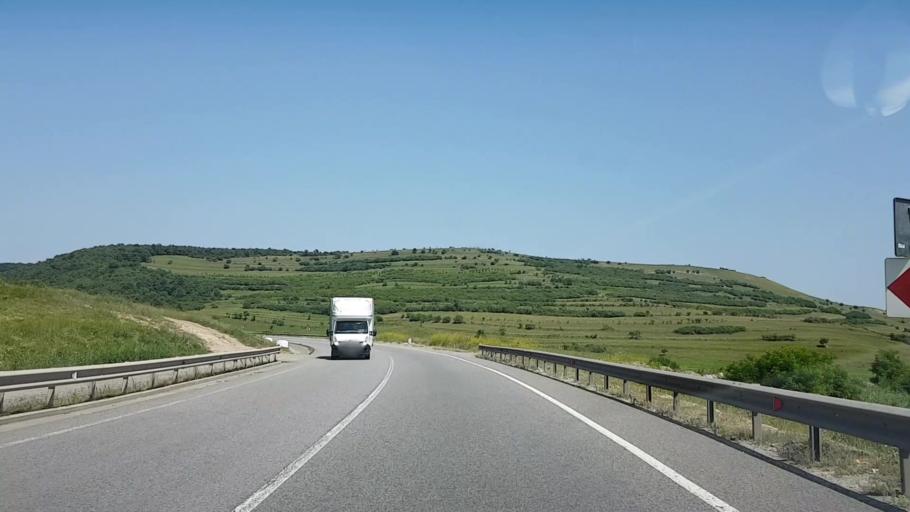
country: RO
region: Cluj
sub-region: Comuna Feleacu
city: Gheorghieni
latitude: 46.7325
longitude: 23.7032
